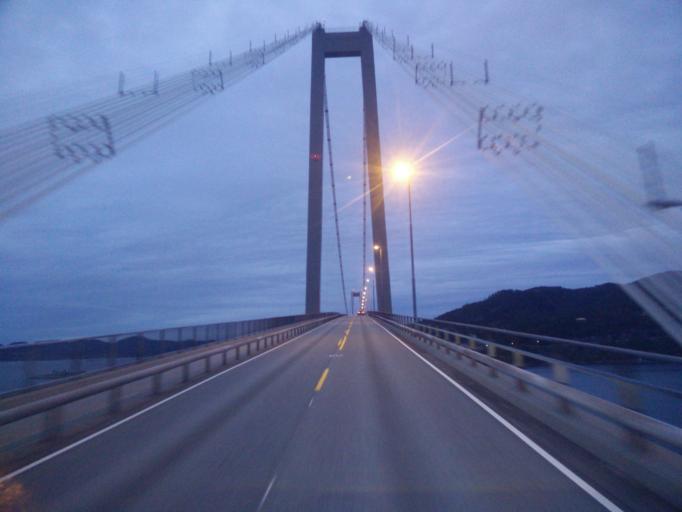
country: NO
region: More og Romsdal
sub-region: Gjemnes
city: Batnfjordsora
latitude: 62.9680
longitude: 7.7746
